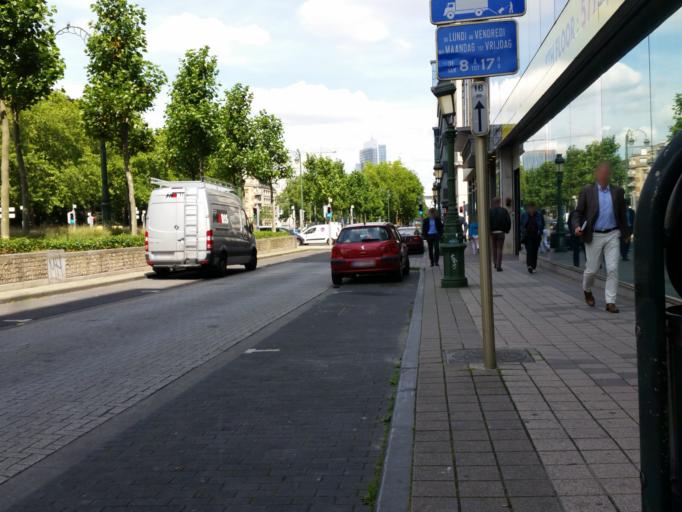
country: BE
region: Brussels Capital
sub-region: Bruxelles-Capitale
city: Brussels
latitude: 50.8410
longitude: 4.3667
